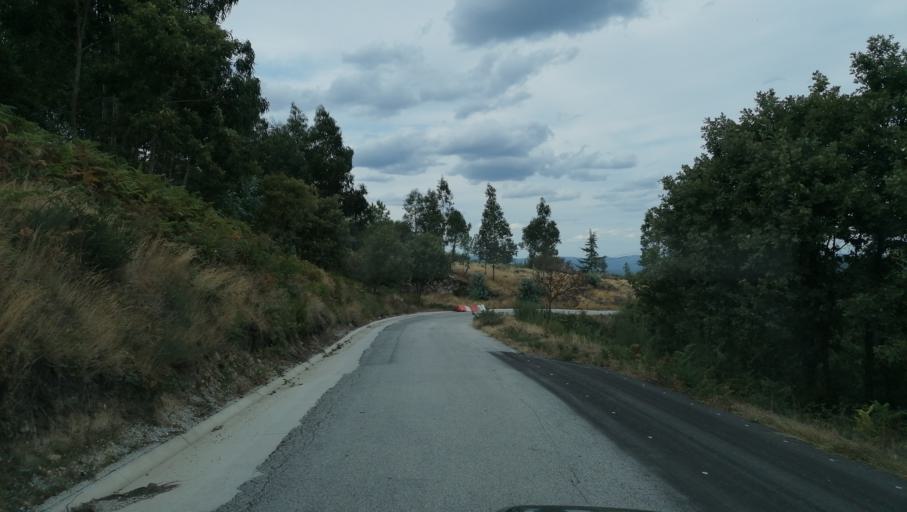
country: PT
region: Vila Real
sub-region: Vila Pouca de Aguiar
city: Vila Pouca de Aguiar
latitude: 41.5606
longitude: -7.6832
